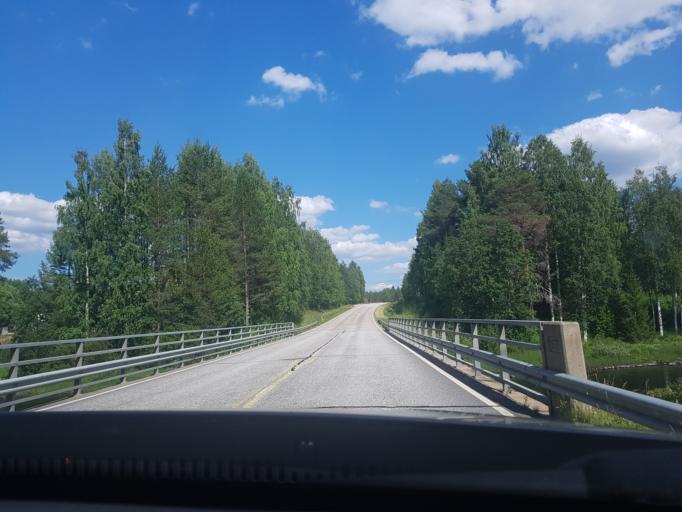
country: FI
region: Kainuu
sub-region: Kehys-Kainuu
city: Kuhmo
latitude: 64.2009
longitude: 29.6948
